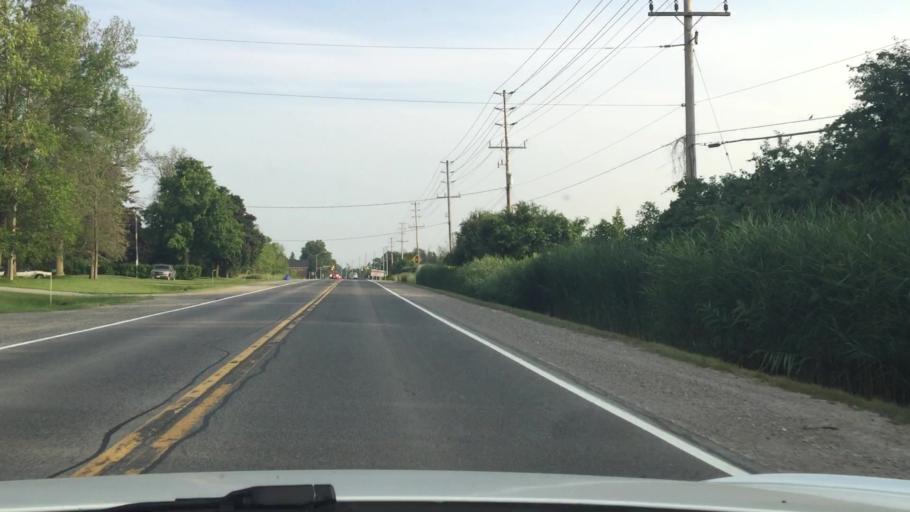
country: CA
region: Ontario
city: Oshawa
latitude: 43.9004
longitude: -78.7729
